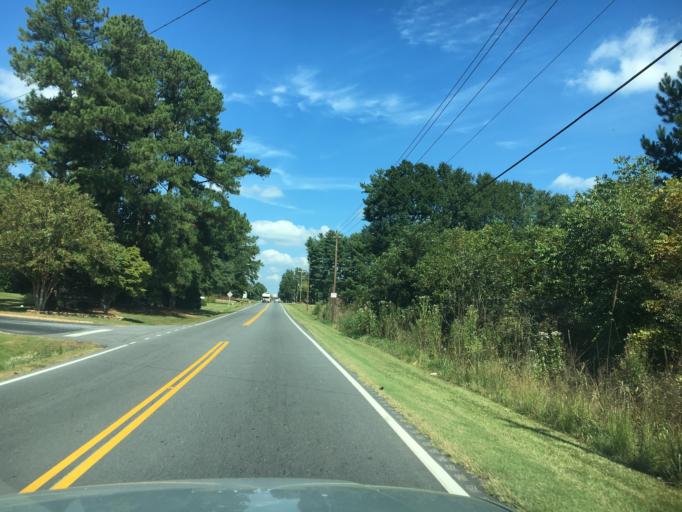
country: US
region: South Carolina
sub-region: Spartanburg County
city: Valley Falls
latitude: 35.0155
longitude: -81.9486
